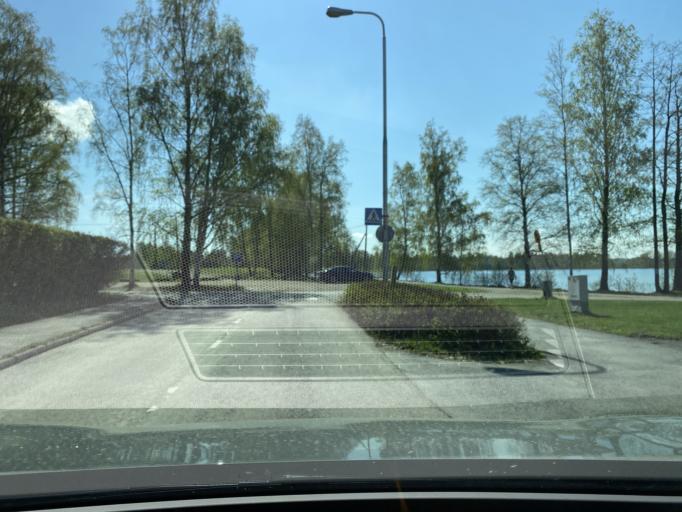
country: FI
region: Pirkanmaa
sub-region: Lounais-Pirkanmaa
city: Vammala
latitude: 61.3364
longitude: 22.9120
